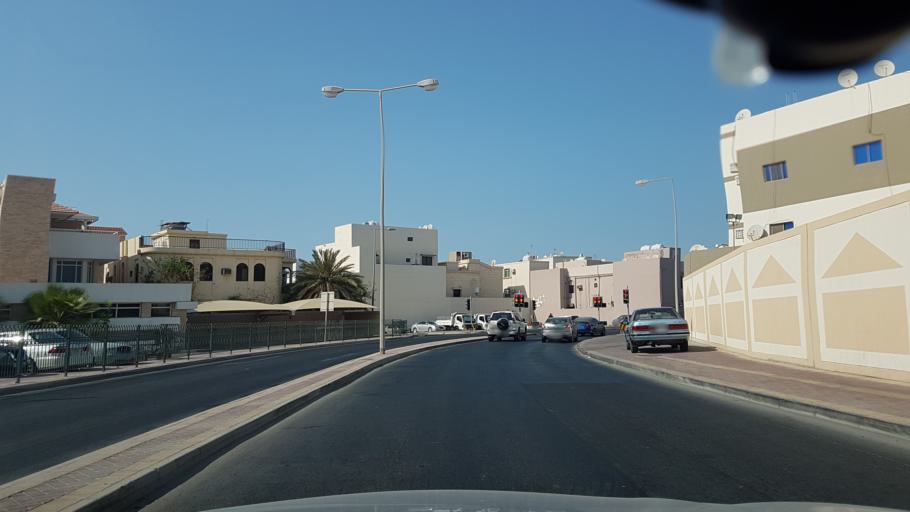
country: BH
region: Muharraq
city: Al Hadd
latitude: 26.2570
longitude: 50.6366
